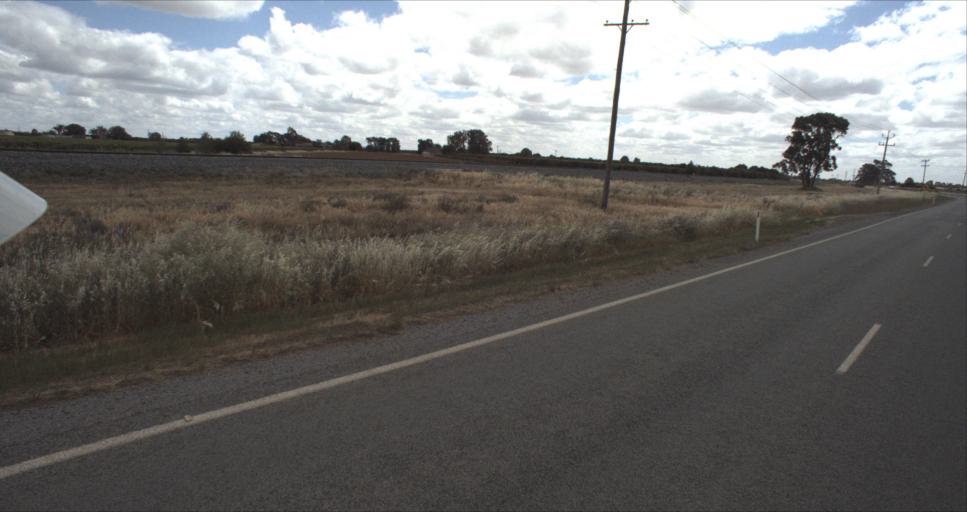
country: AU
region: New South Wales
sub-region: Leeton
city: Leeton
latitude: -34.5826
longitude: 146.4015
